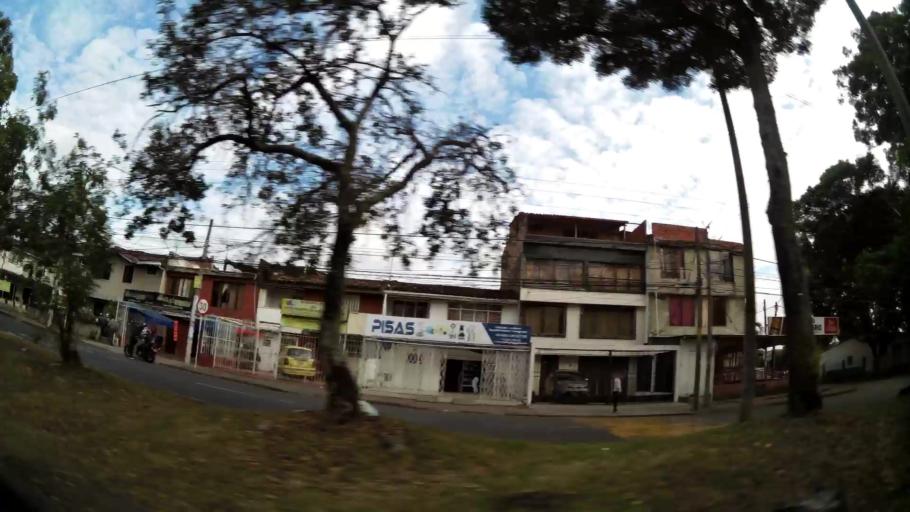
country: CO
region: Valle del Cauca
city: Cali
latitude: 3.4686
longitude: -76.5004
